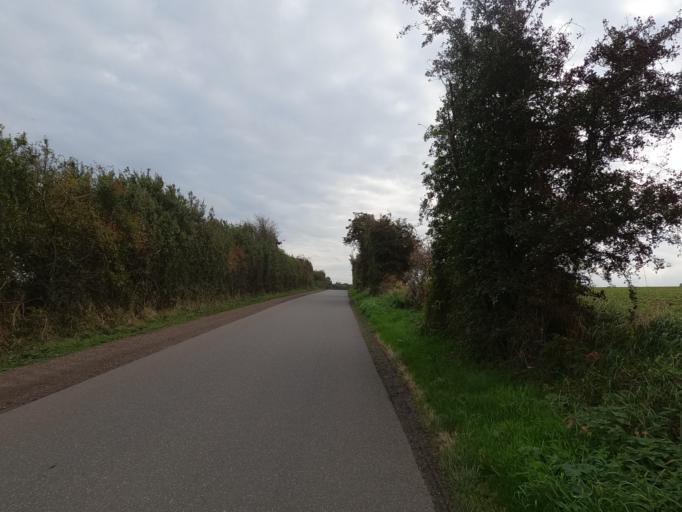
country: DE
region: Schleswig-Holstein
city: Neukirchen
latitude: 54.3562
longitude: 11.0316
